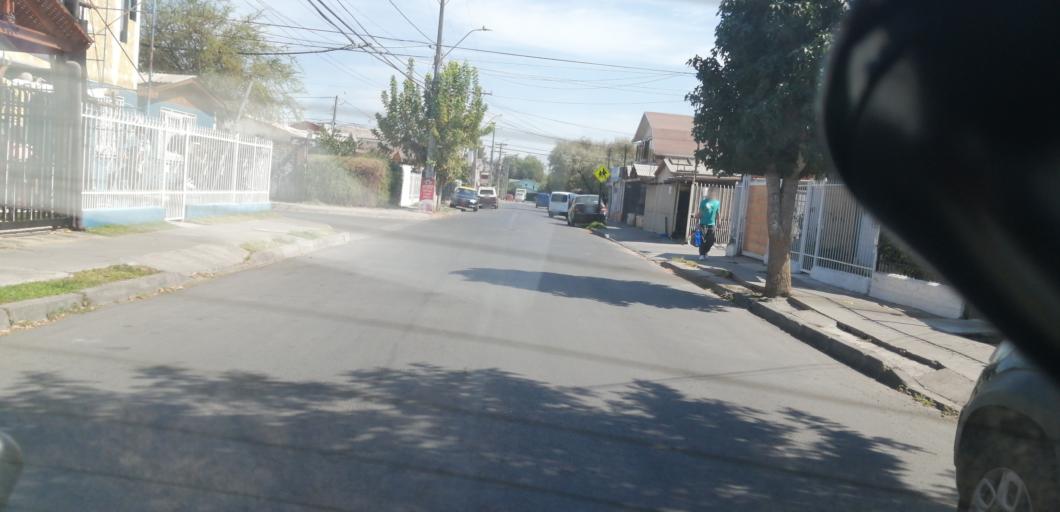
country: CL
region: Santiago Metropolitan
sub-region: Provincia de Santiago
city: Lo Prado
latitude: -33.4656
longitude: -70.7406
